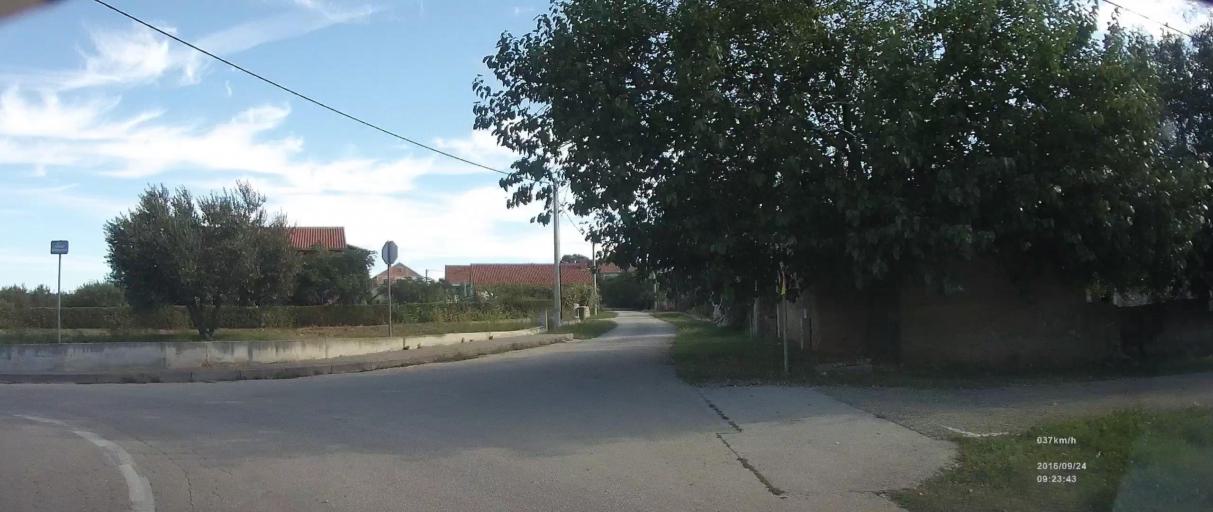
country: HR
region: Zadarska
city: Polaca
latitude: 44.0754
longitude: 15.4768
